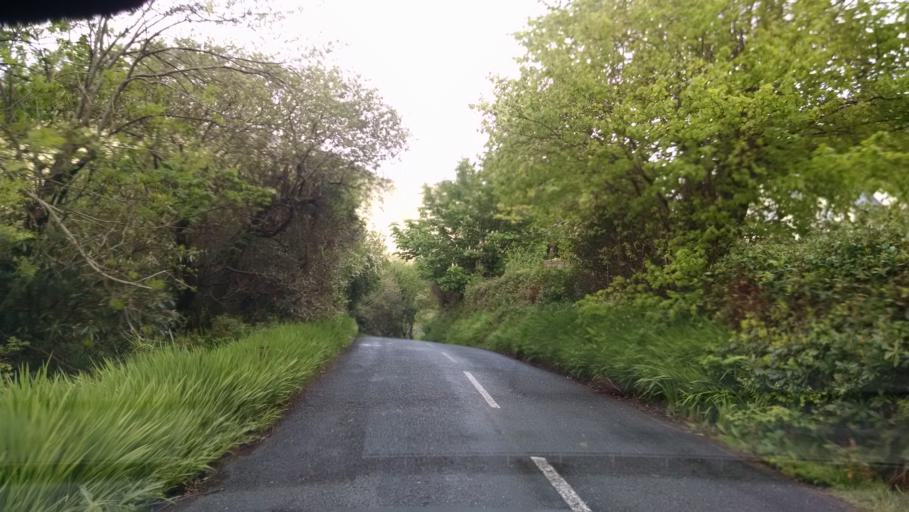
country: IE
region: Connaught
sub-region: Maigh Eo
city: Westport
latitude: 53.6170
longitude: -9.6708
